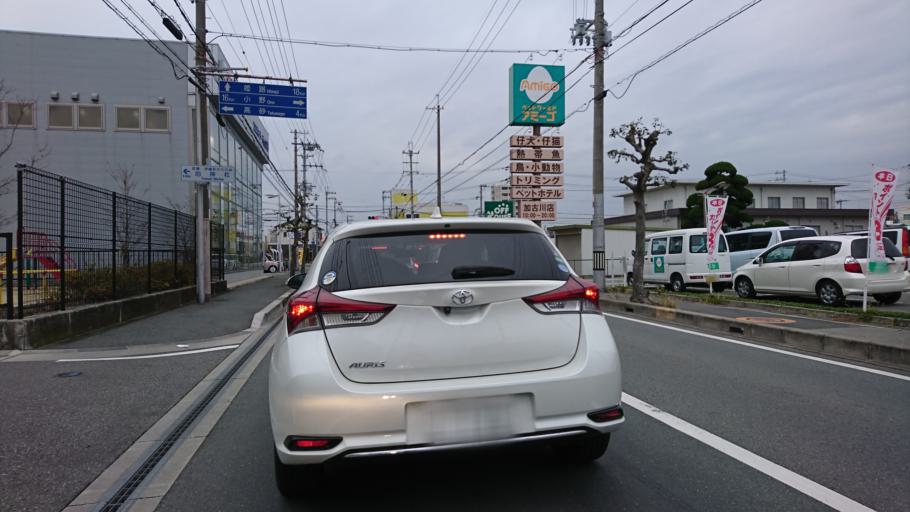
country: JP
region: Hyogo
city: Kakogawacho-honmachi
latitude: 34.7622
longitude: 134.8318
